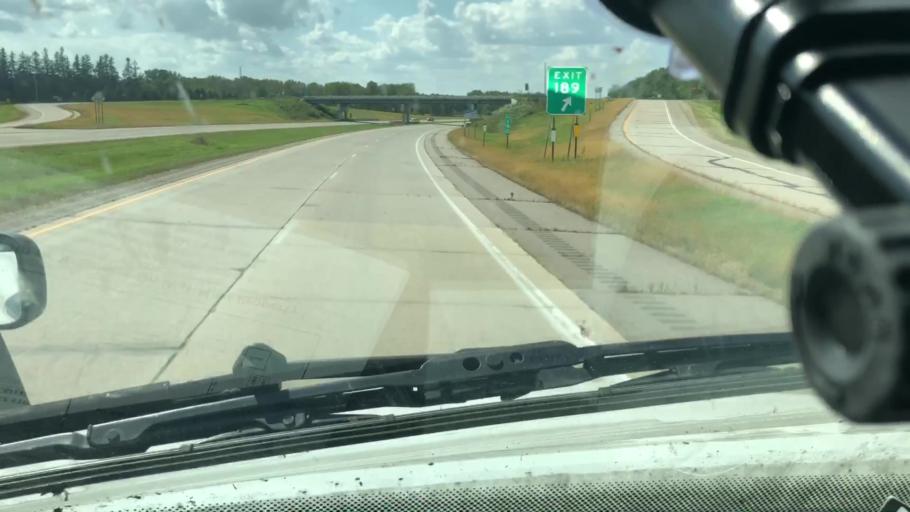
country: US
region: Minnesota
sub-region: Mower County
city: Grand Meadow
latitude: 43.6767
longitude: -92.7474
